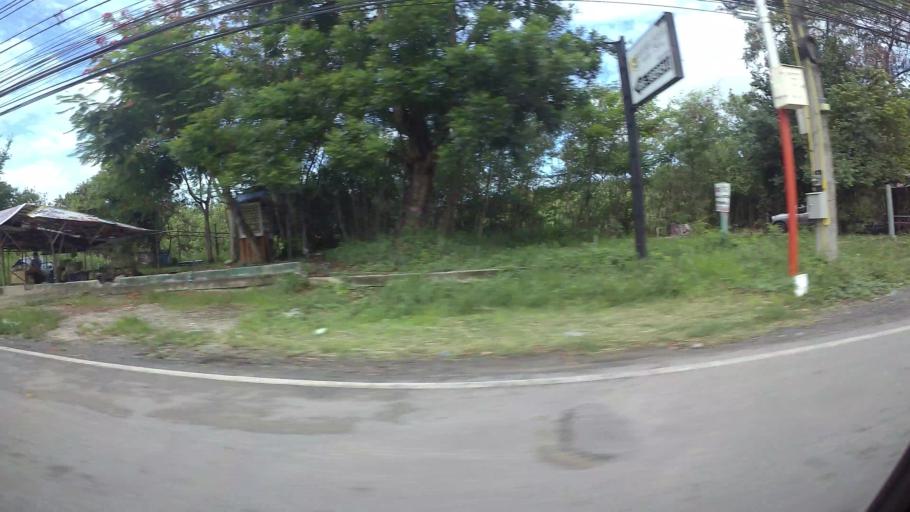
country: TH
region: Rayong
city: Rayong
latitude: 12.7076
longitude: 101.1779
